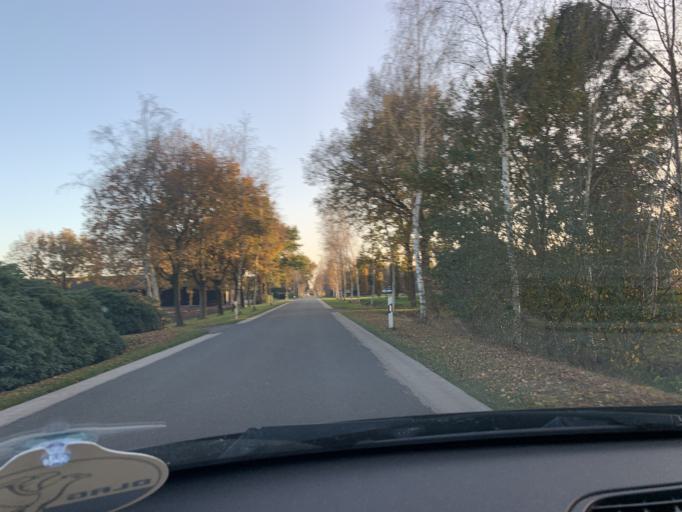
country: DE
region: Lower Saxony
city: Bad Zwischenahn
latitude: 53.1528
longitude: 8.0520
